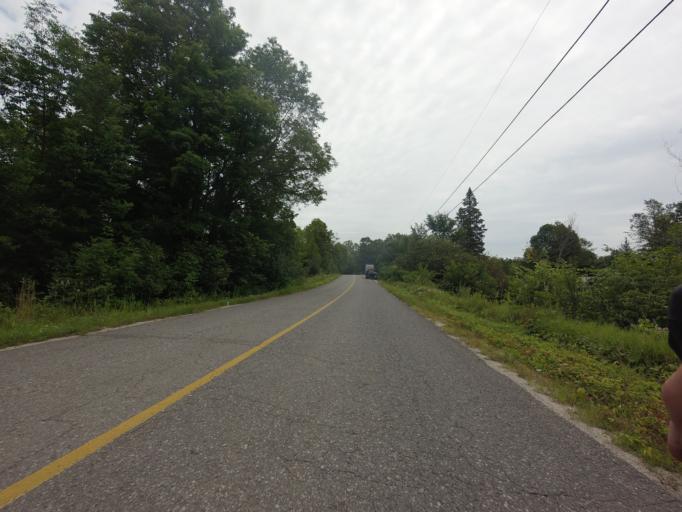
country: CA
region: Ontario
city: Perth
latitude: 44.6759
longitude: -76.6590
